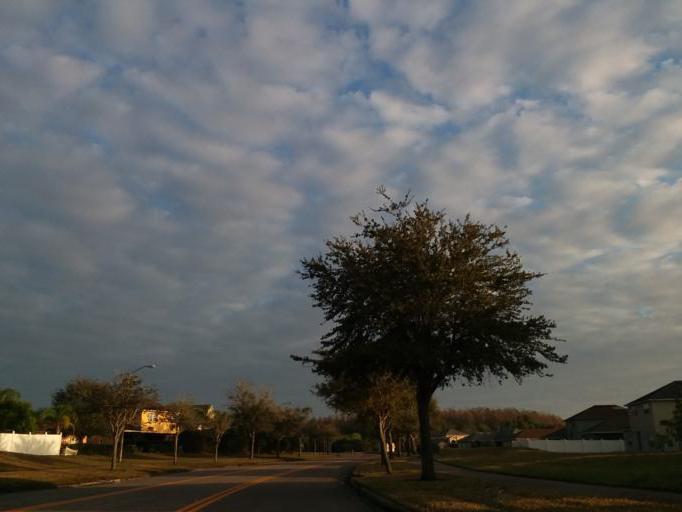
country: US
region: Florida
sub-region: Osceola County
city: Campbell
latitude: 28.2199
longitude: -81.4543
